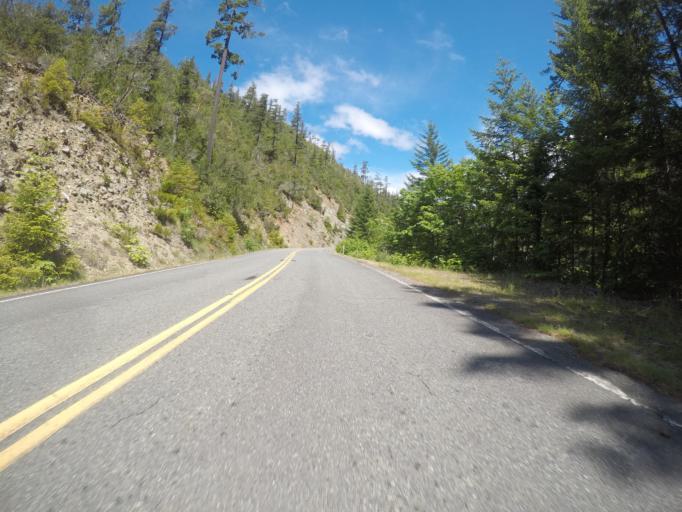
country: US
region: California
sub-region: Del Norte County
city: Bertsch-Oceanview
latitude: 41.7062
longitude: -123.9401
